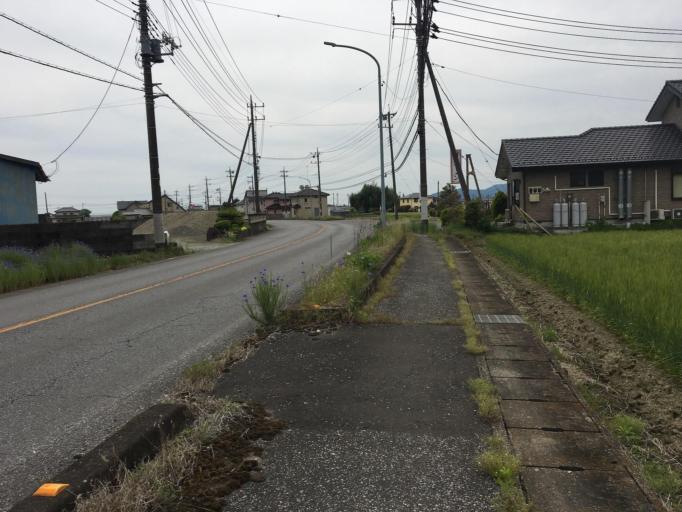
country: JP
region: Tochigi
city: Mibu
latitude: 36.4374
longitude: 139.7505
